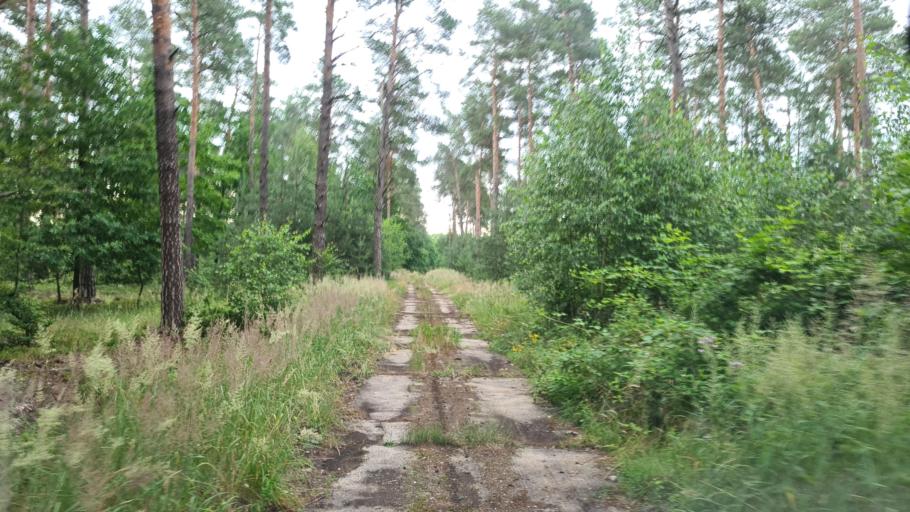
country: DE
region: Brandenburg
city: Crinitz
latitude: 51.7186
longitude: 13.7317
